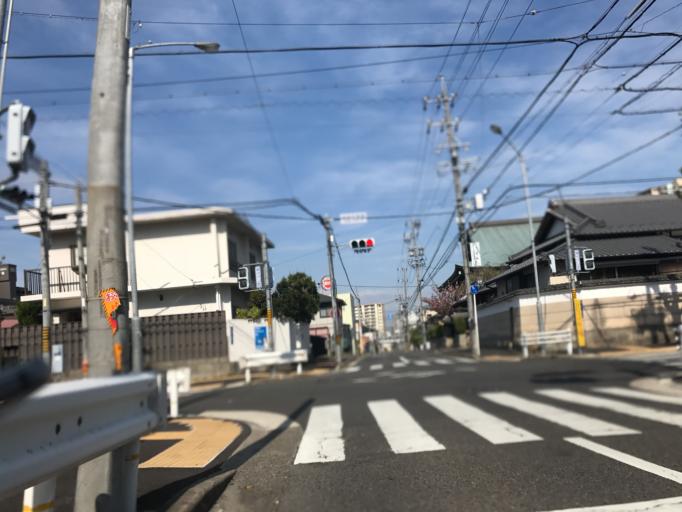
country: JP
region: Aichi
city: Nagoya-shi
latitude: 35.1662
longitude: 136.9326
